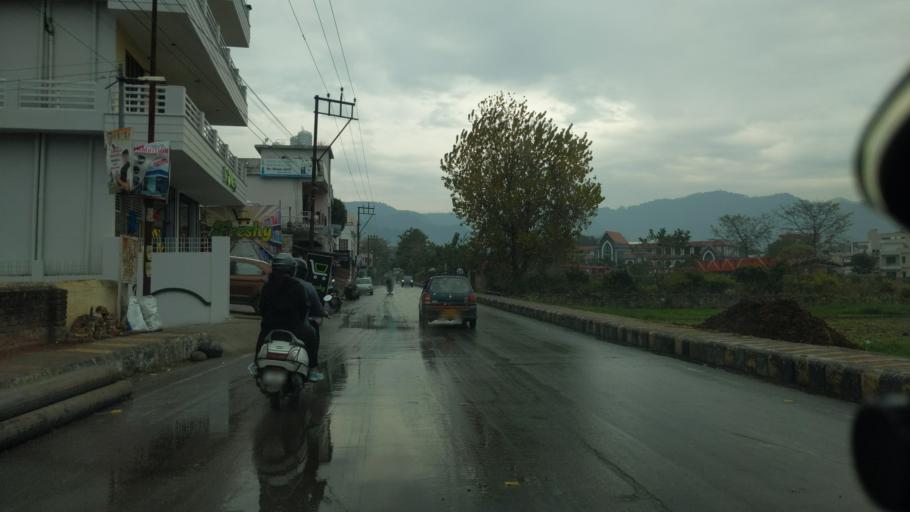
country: IN
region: Uttarakhand
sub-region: Naini Tal
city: Haldwani
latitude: 29.2443
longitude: 79.5317
